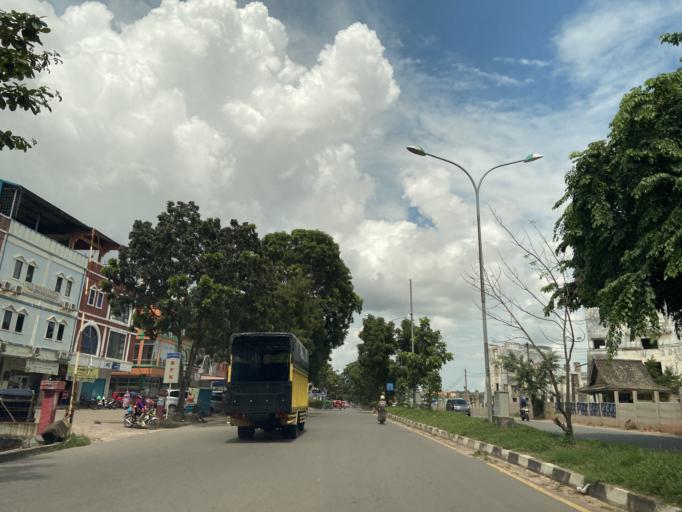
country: SG
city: Singapore
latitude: 1.1483
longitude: 104.0034
